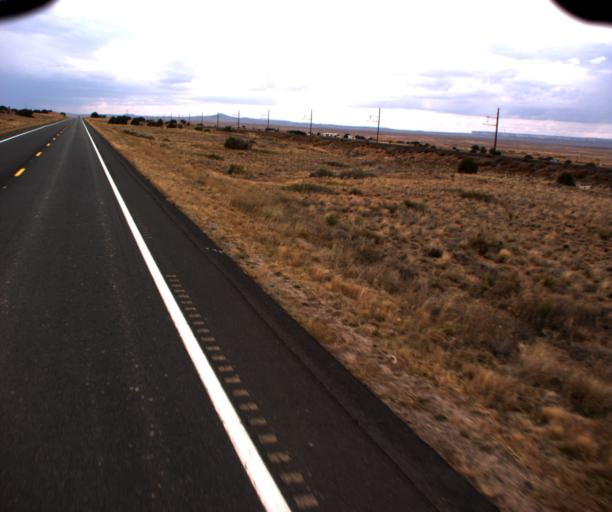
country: US
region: Arizona
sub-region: Coconino County
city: Kaibito
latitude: 36.4127
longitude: -110.8226
